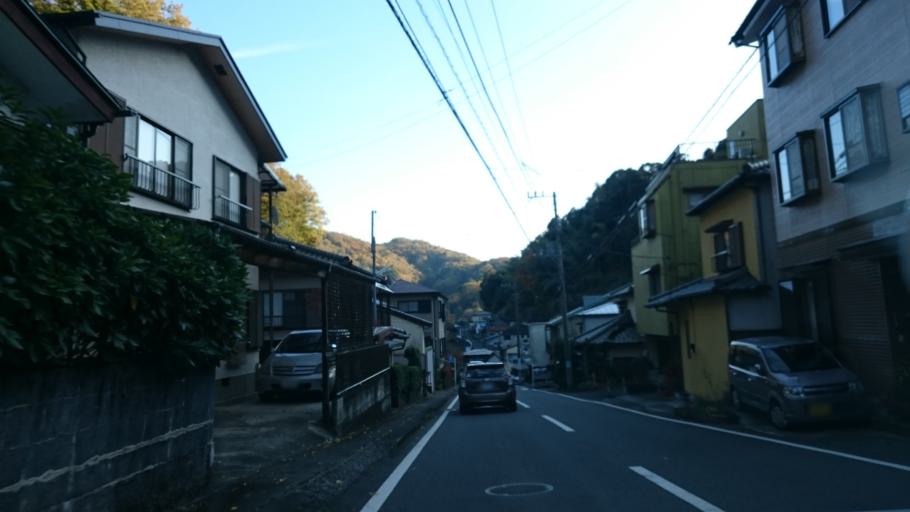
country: JP
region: Shizuoka
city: Numazu
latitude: 34.9750
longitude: 138.9281
